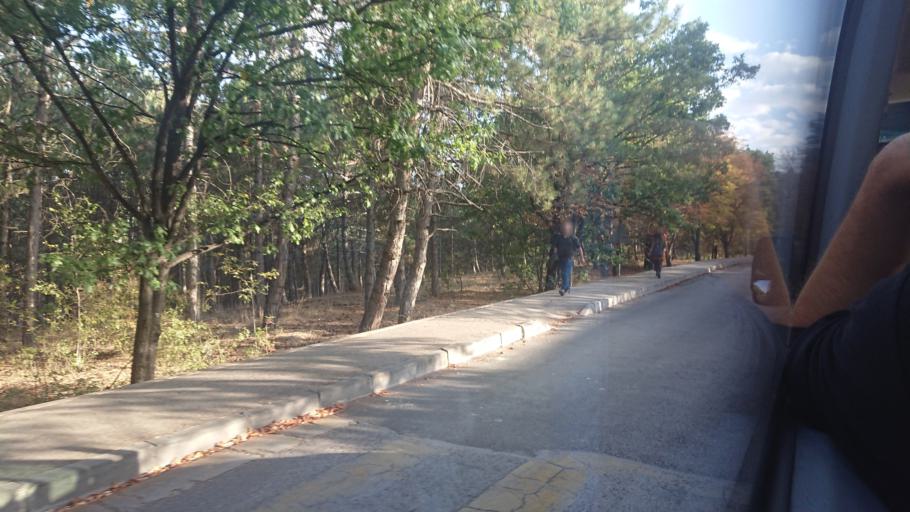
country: TR
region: Ankara
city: Ankara
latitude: 39.8884
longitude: 32.7843
